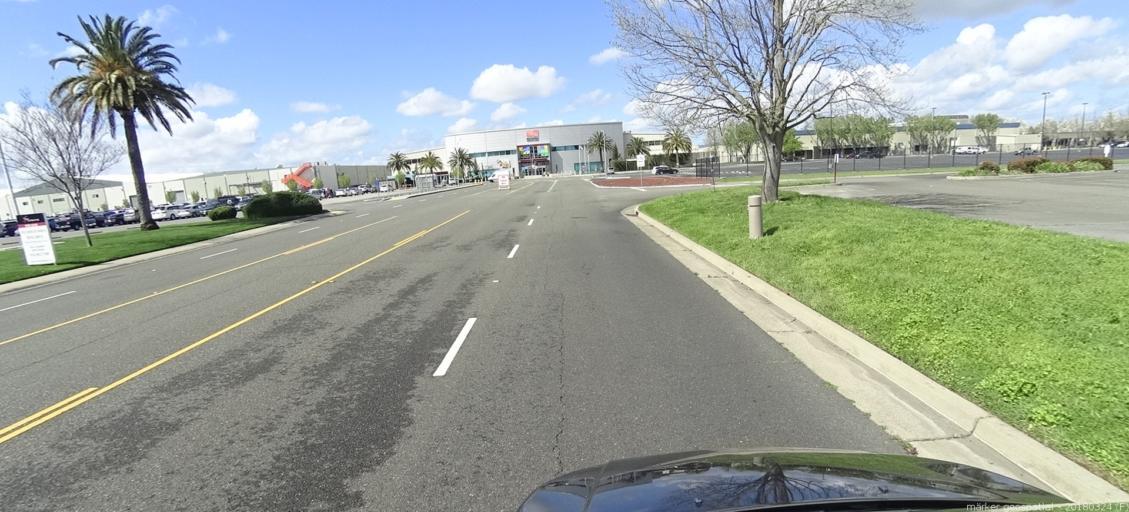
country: US
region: California
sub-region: Sacramento County
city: North Highlands
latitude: 38.6656
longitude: -121.3891
